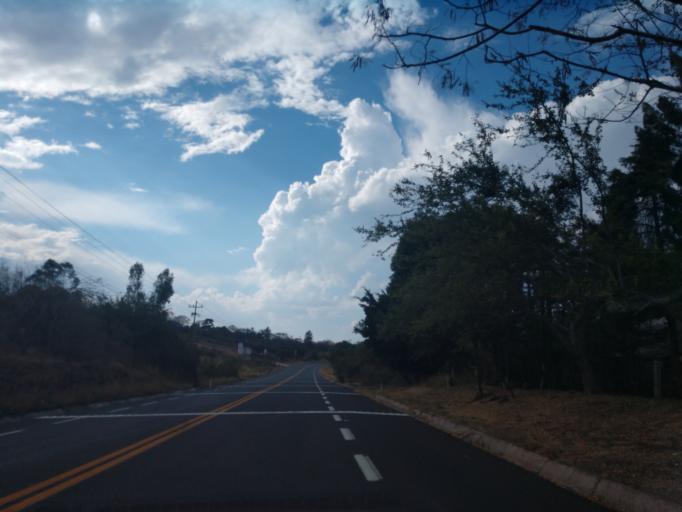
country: MX
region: Jalisco
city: Ajijic
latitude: 20.1863
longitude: -103.2519
